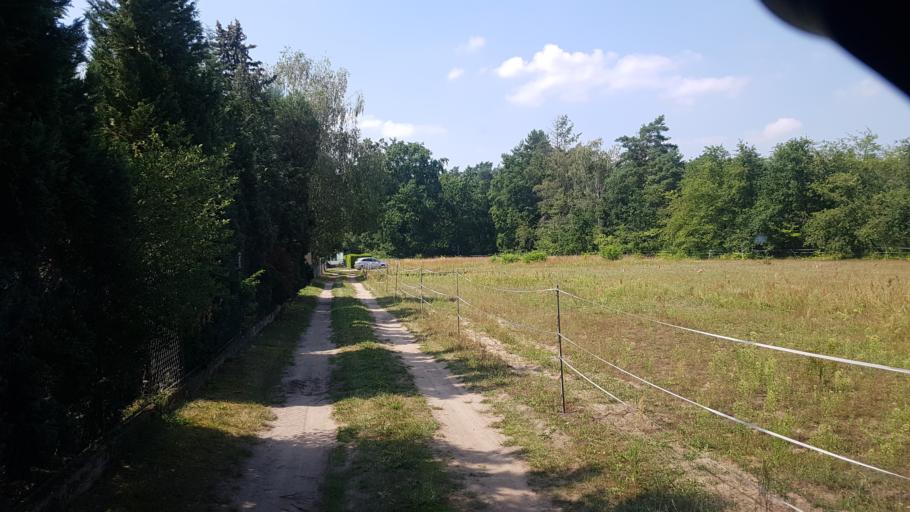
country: DE
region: Brandenburg
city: Cottbus
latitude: 51.6820
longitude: 14.4085
